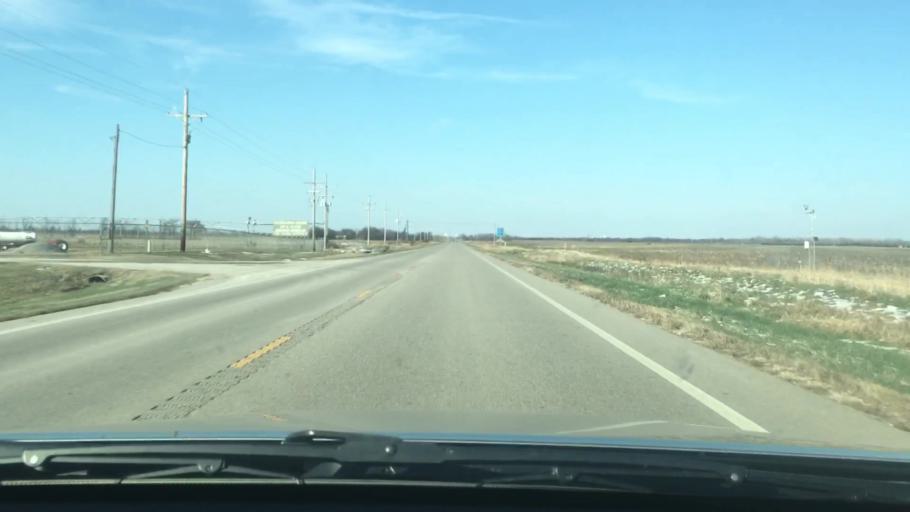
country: US
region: Kansas
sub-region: Rice County
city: Lyons
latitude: 38.2776
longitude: -98.2019
